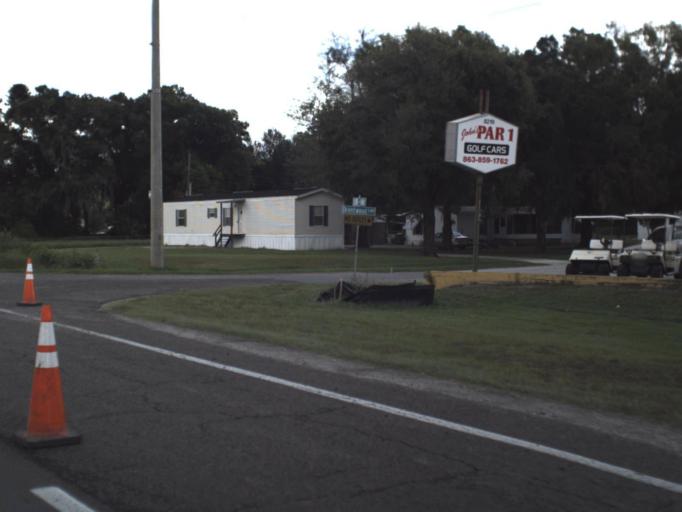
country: US
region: Florida
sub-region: Polk County
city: Gibsonia
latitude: 28.1488
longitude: -81.9736
